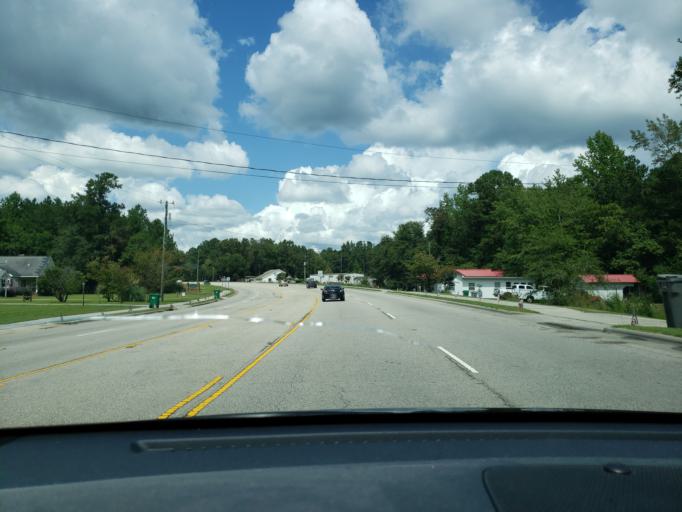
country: US
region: North Carolina
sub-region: Bladen County
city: Elizabethtown
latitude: 34.6624
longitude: -78.7269
